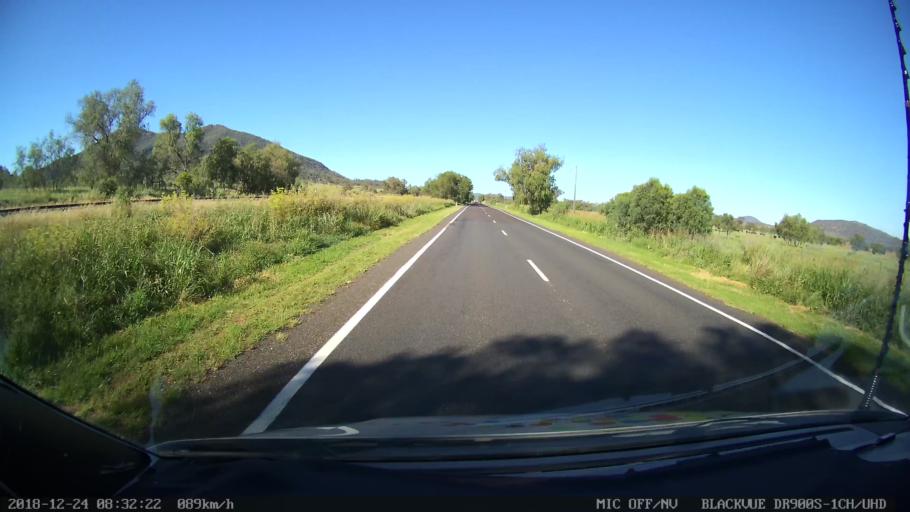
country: AU
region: New South Wales
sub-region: Tamworth Municipality
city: Phillip
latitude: -31.2796
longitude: 150.6989
